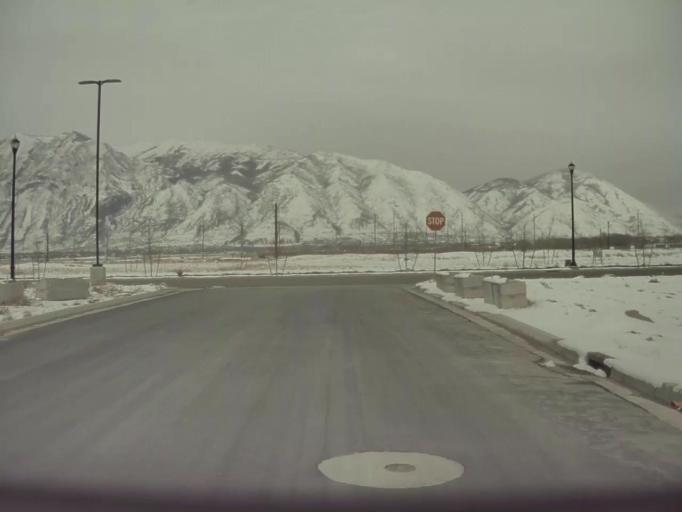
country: US
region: Utah
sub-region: Utah County
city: Spanish Fork
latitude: 40.1274
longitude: -111.6395
